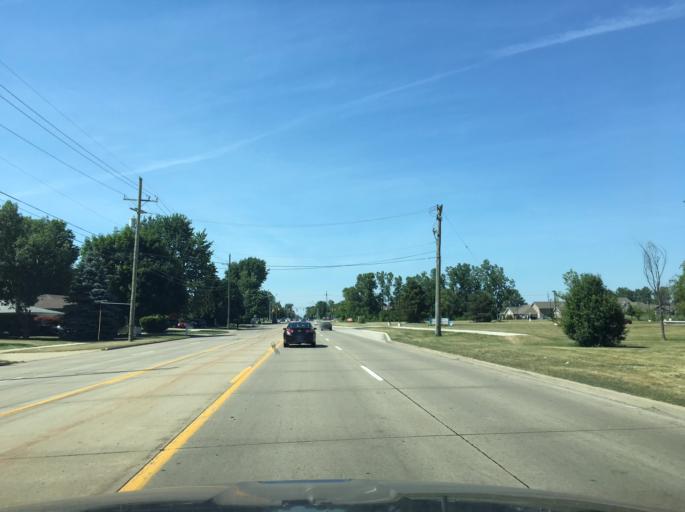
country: US
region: Michigan
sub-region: Macomb County
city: Utica
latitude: 42.6385
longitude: -82.9934
